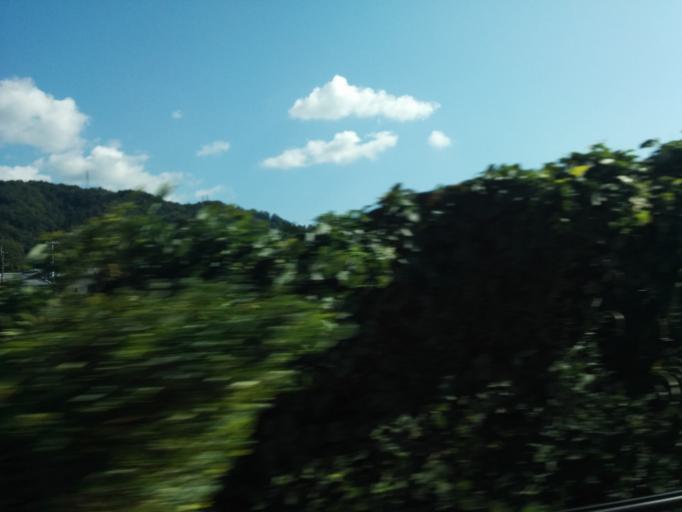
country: JP
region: Shiga Prefecture
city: Hikone
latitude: 35.2554
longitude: 136.2752
